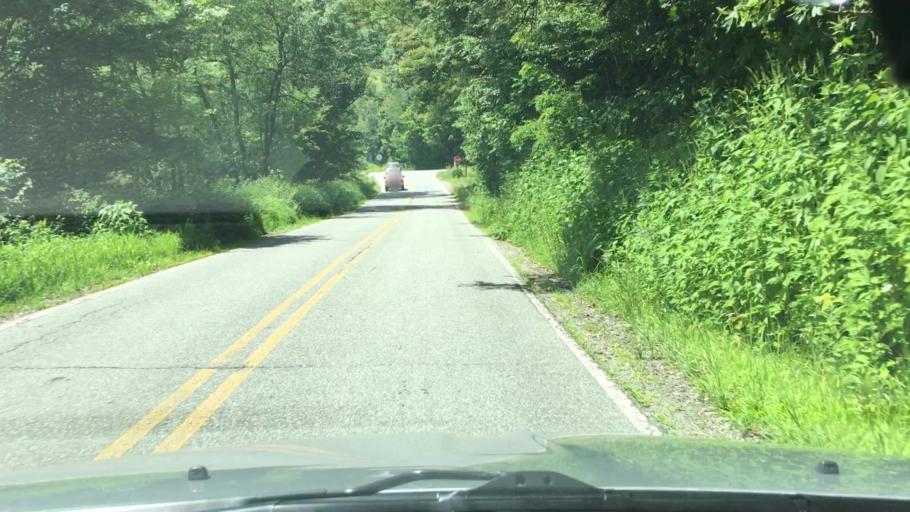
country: US
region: North Carolina
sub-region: Madison County
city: Mars Hill
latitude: 35.9080
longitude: -82.5461
